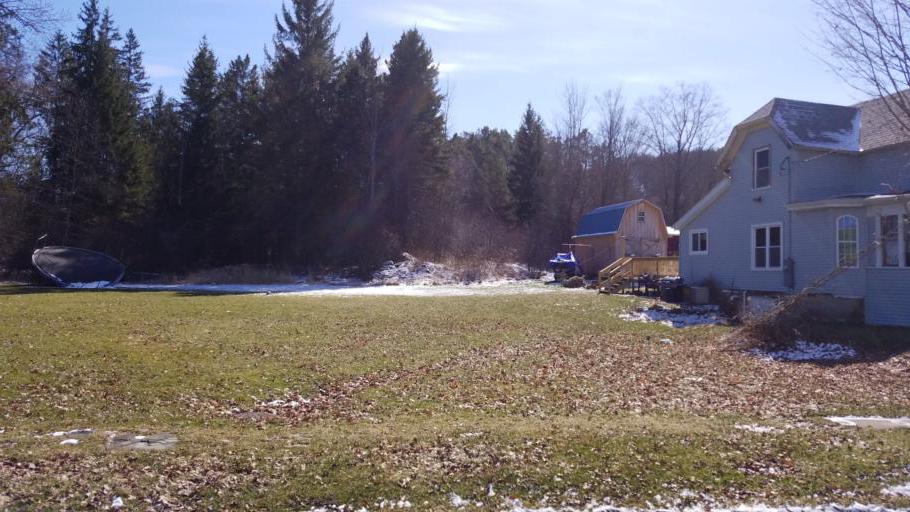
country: US
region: New York
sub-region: Allegany County
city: Wellsville
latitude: 42.1193
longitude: -77.9569
